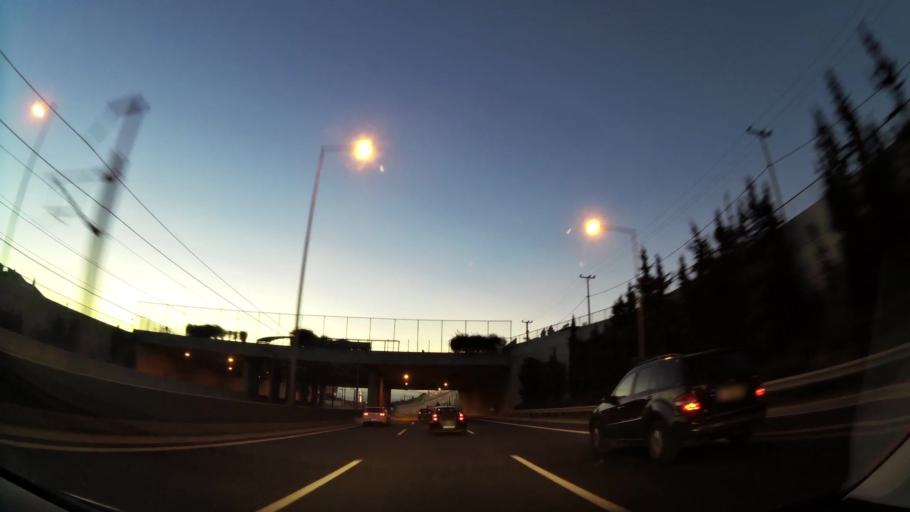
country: GR
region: Attica
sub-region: Nomarchia Anatolikis Attikis
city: Gerakas
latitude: 38.0206
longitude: 23.8595
